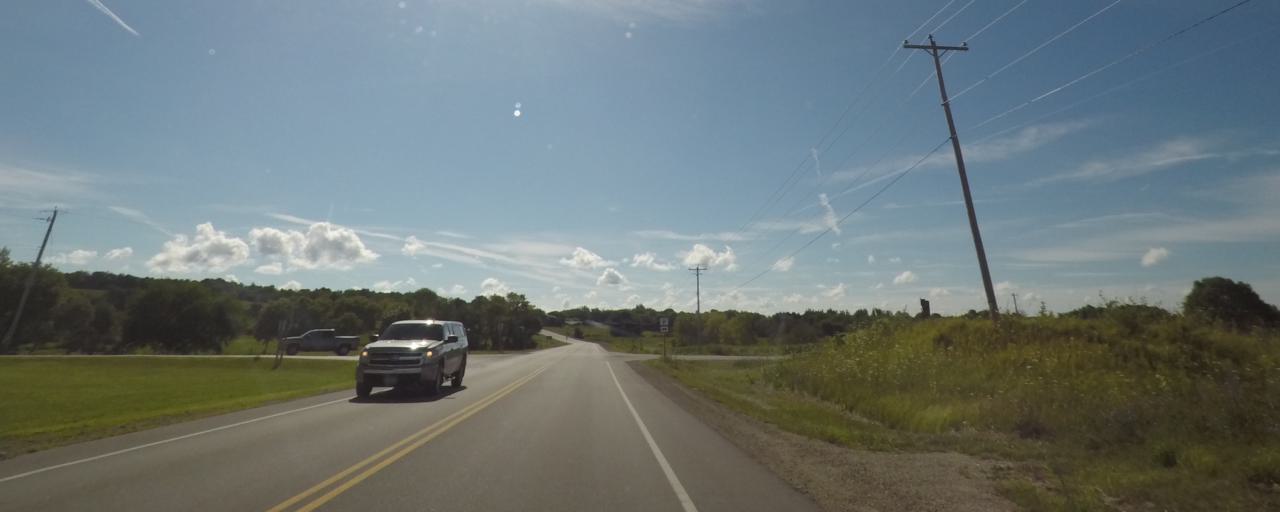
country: US
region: Wisconsin
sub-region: Jefferson County
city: Ixonia
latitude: 43.0753
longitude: -88.6654
